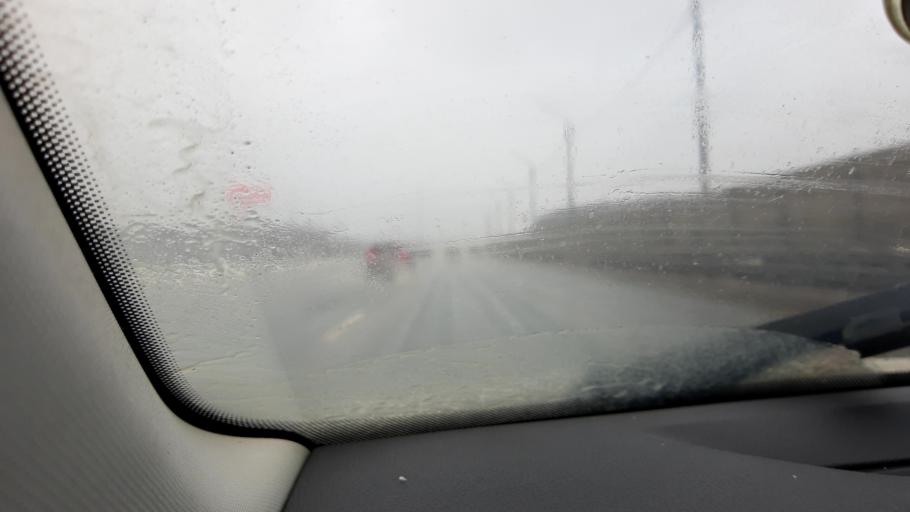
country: RU
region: Moskovskaya
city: Rozhdestveno
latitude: 55.8190
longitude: 36.9728
